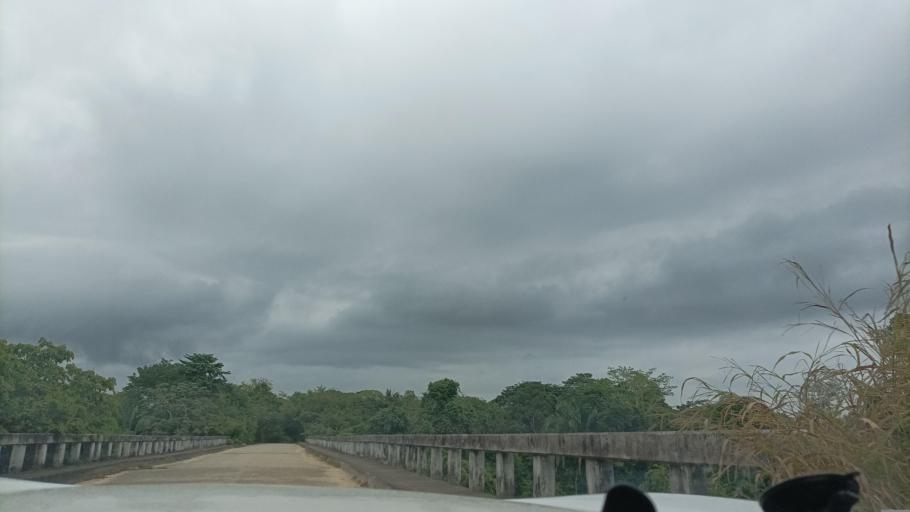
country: MX
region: Veracruz
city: Hidalgotitlan
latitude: 17.6470
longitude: -94.5035
